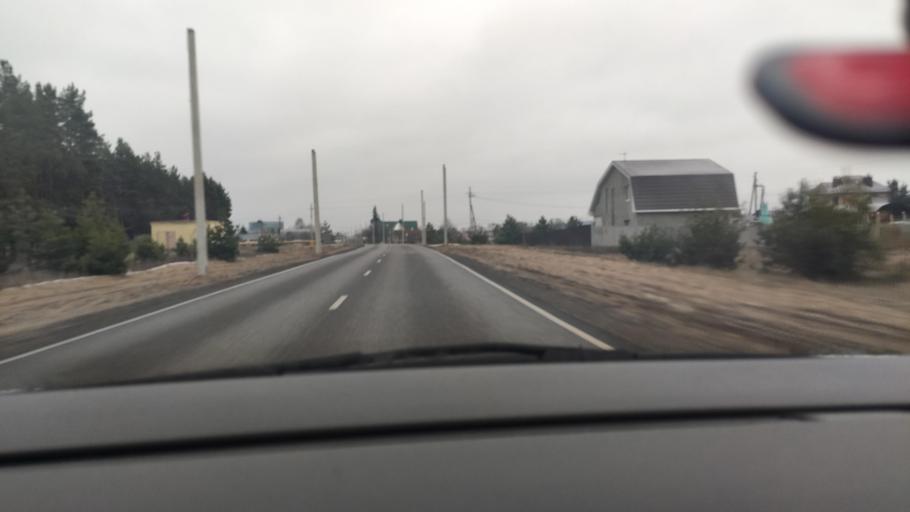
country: RU
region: Voronezj
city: Shilovo
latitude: 51.5844
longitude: 39.0339
